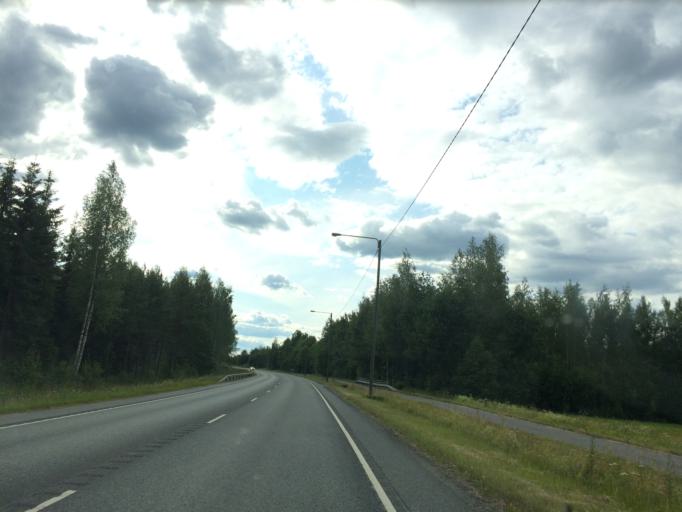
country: FI
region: Haeme
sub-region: Haemeenlinna
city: Janakkala
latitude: 60.9225
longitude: 24.5980
